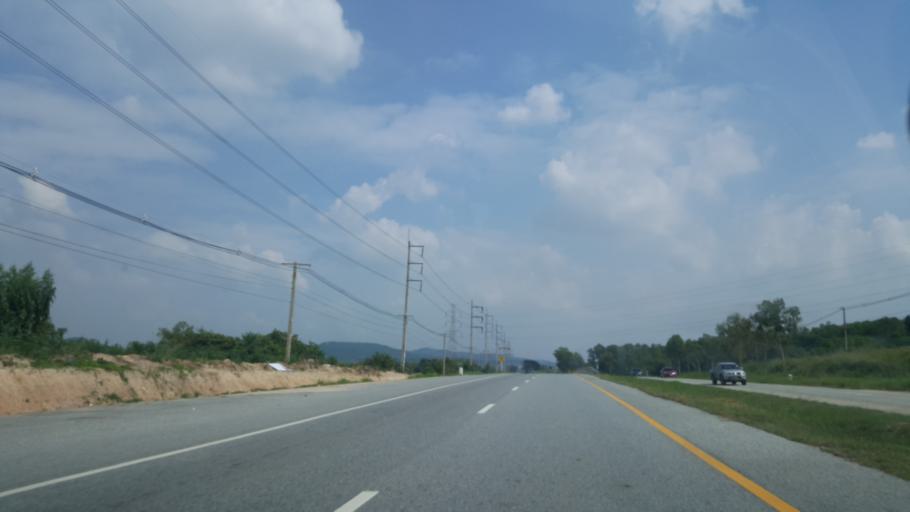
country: TH
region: Chon Buri
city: Ban Talat Bueng
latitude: 12.9264
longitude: 101.0342
